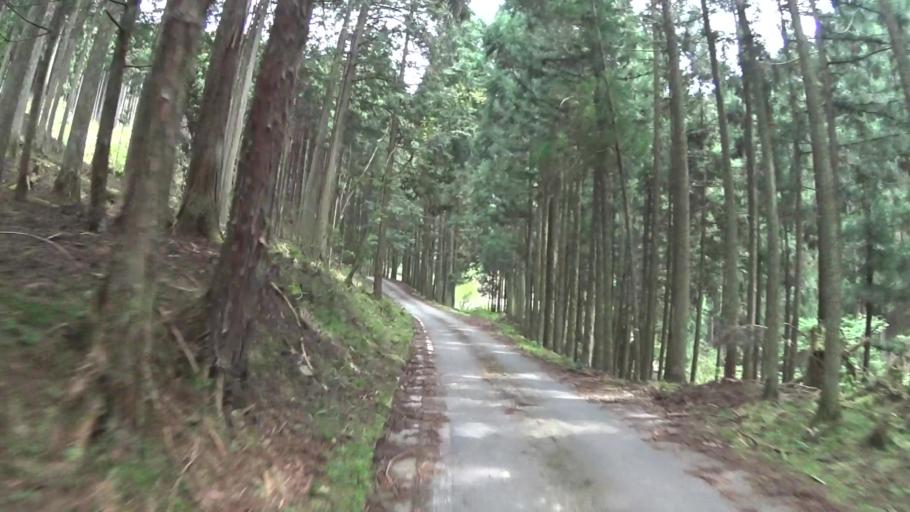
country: JP
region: Kyoto
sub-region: Kyoto-shi
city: Kamigyo-ku
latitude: 35.1864
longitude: 135.7046
